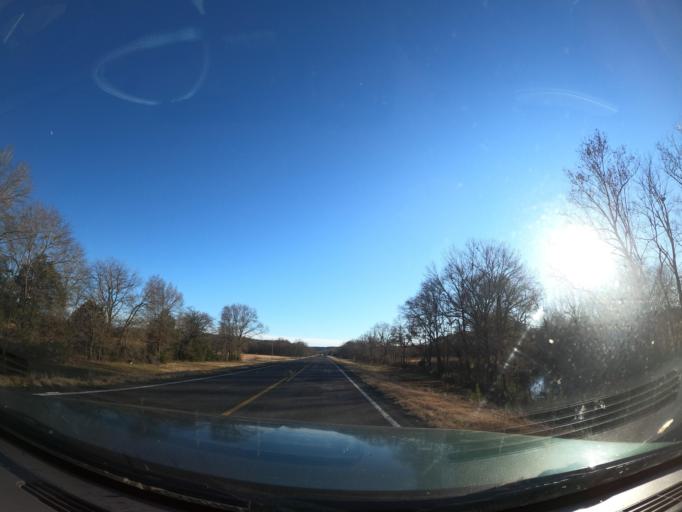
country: US
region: Oklahoma
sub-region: Latimer County
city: Wilburton
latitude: 34.9462
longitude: -95.3413
